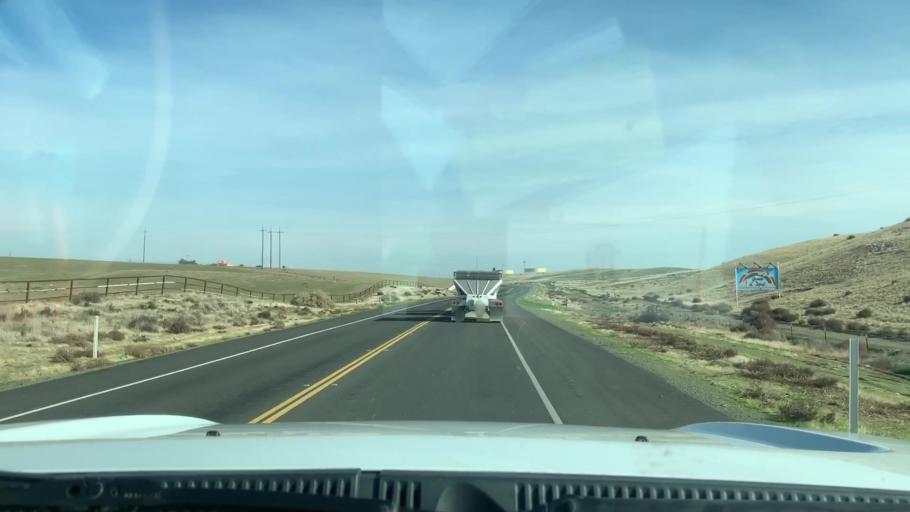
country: US
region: California
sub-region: Fresno County
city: Coalinga
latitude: 36.2021
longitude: -120.3214
